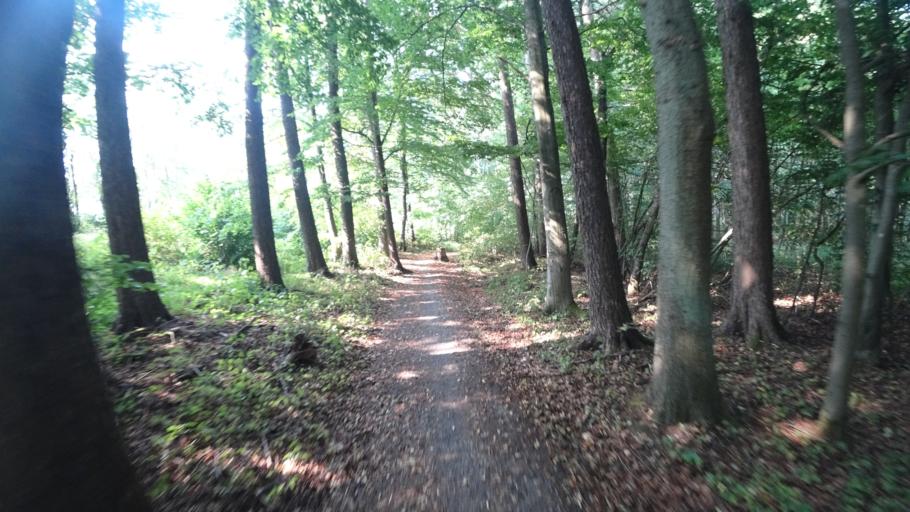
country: DE
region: Rheinland-Pfalz
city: Hundsdorf
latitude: 50.4563
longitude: 7.7087
